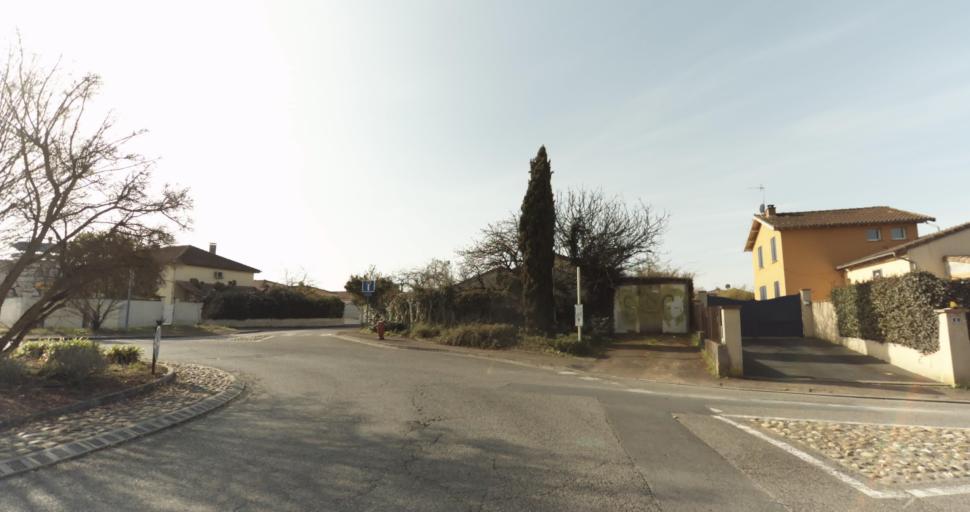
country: FR
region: Midi-Pyrenees
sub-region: Departement du Tarn
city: Saint-Sulpice-la-Pointe
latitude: 43.7677
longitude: 1.6906
